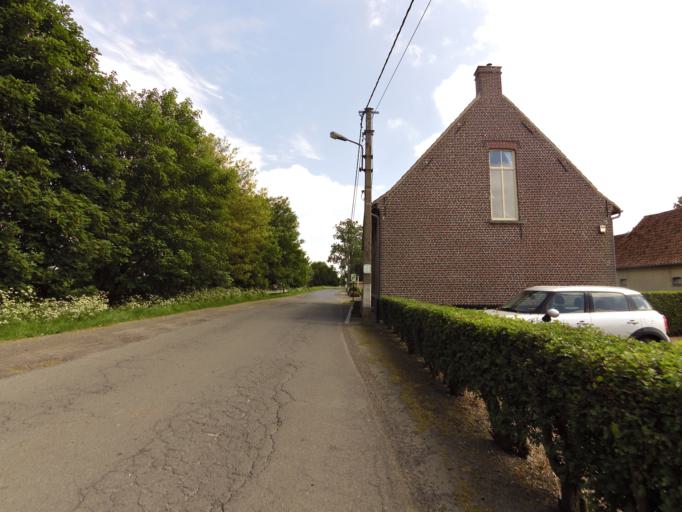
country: BE
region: Flanders
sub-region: Provincie Oost-Vlaanderen
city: Knesselare
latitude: 51.1134
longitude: 3.3982
